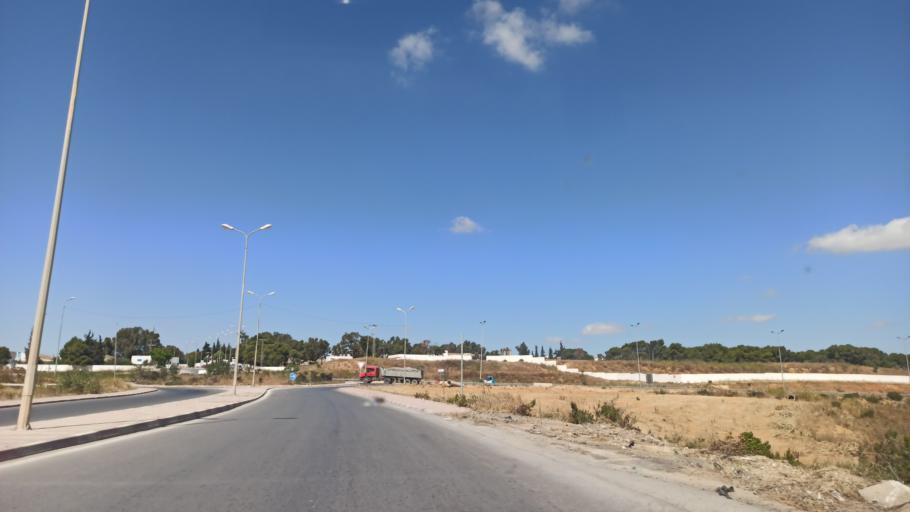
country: TN
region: Manouba
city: Manouba
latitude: 36.7833
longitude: 10.0735
